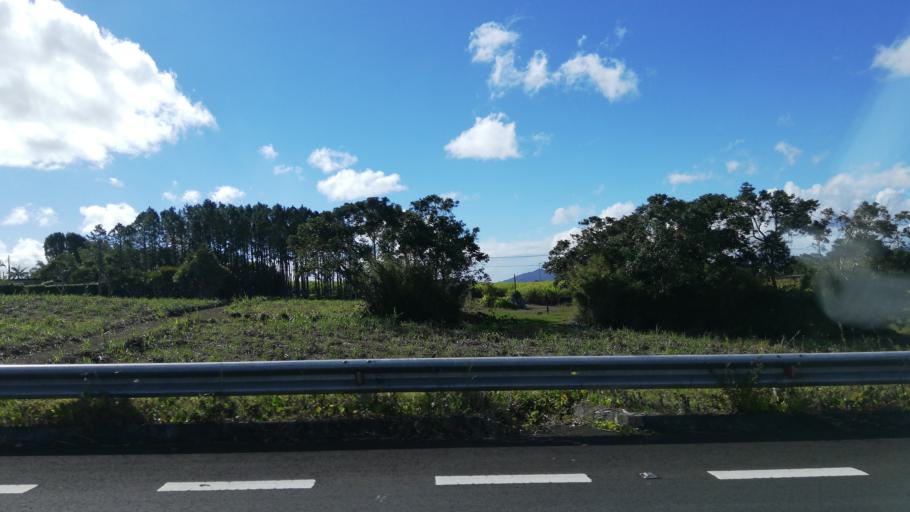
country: MU
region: Moka
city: Quartier Militaire
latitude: -20.2418
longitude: 57.5931
